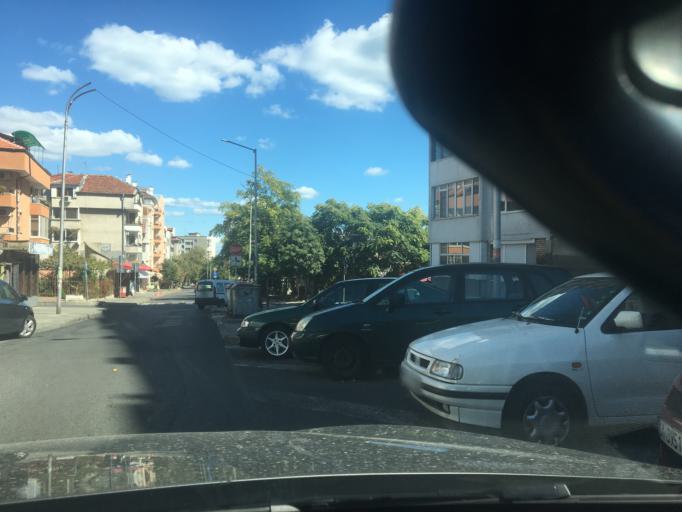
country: BG
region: Burgas
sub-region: Obshtina Burgas
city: Burgas
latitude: 42.5067
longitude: 27.4733
